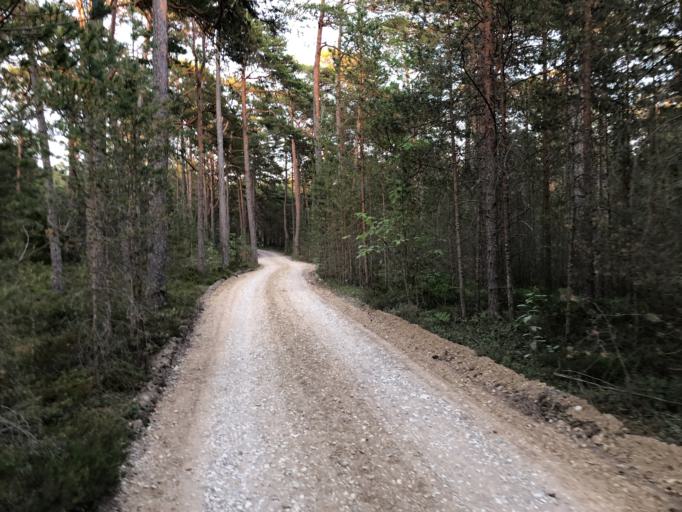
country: EE
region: Harju
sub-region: Paldiski linn
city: Paldiski
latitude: 59.3911
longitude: 24.2251
